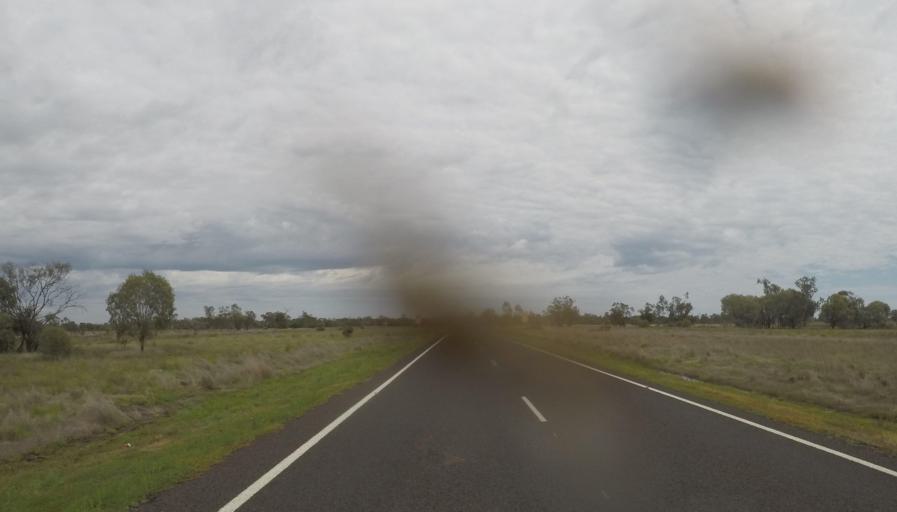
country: AU
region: Queensland
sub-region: Maranoa
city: Roma
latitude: -26.4890
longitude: 148.0657
